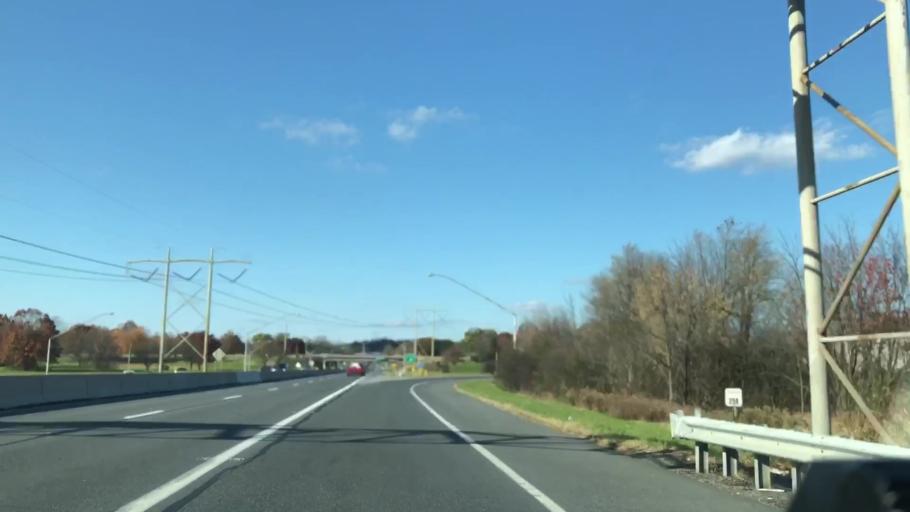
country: US
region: Pennsylvania
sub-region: Lehigh County
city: Wescosville
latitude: 40.5966
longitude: -75.5571
